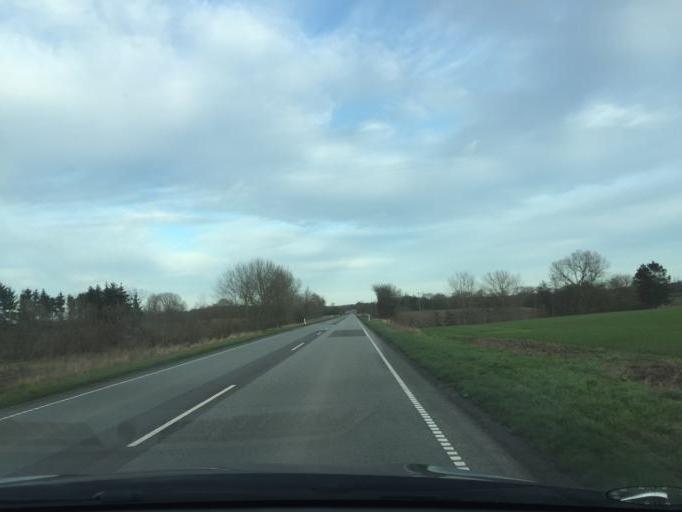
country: DK
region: South Denmark
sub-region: Faaborg-Midtfyn Kommune
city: Ringe
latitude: 55.2147
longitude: 10.4283
